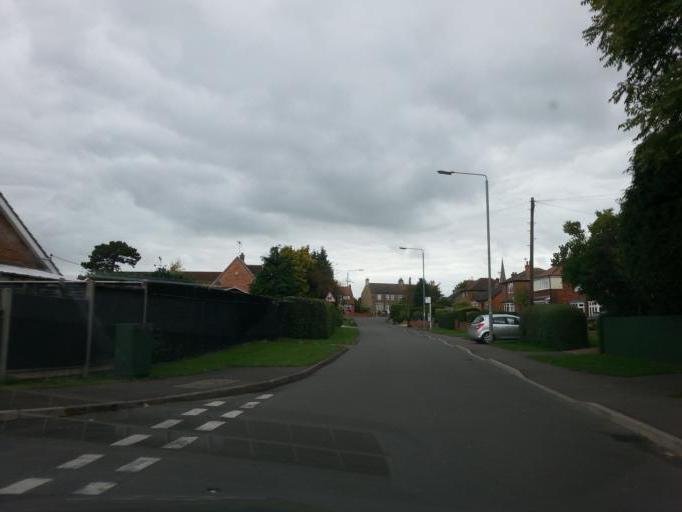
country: GB
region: England
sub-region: Nottinghamshire
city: Newark on Trent
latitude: 53.0523
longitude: -0.7800
